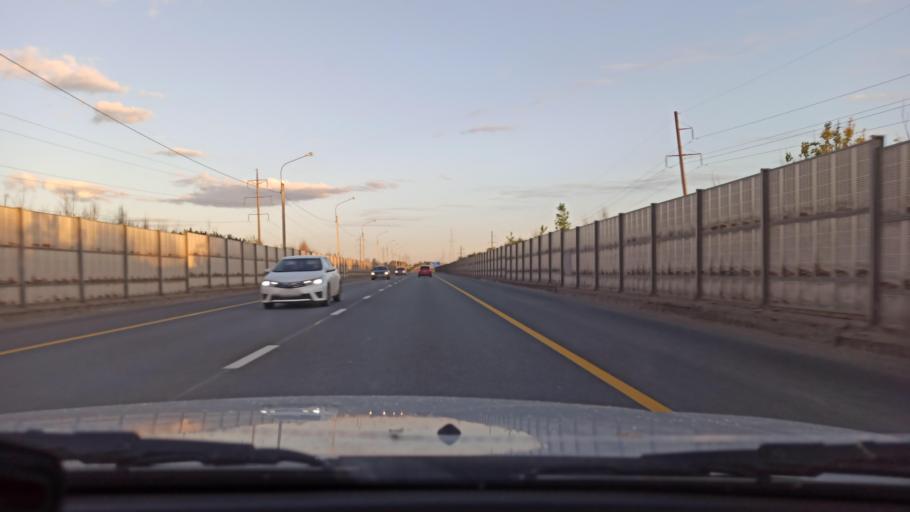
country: RU
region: Vologda
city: Vologda
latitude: 59.2269
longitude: 39.7750
